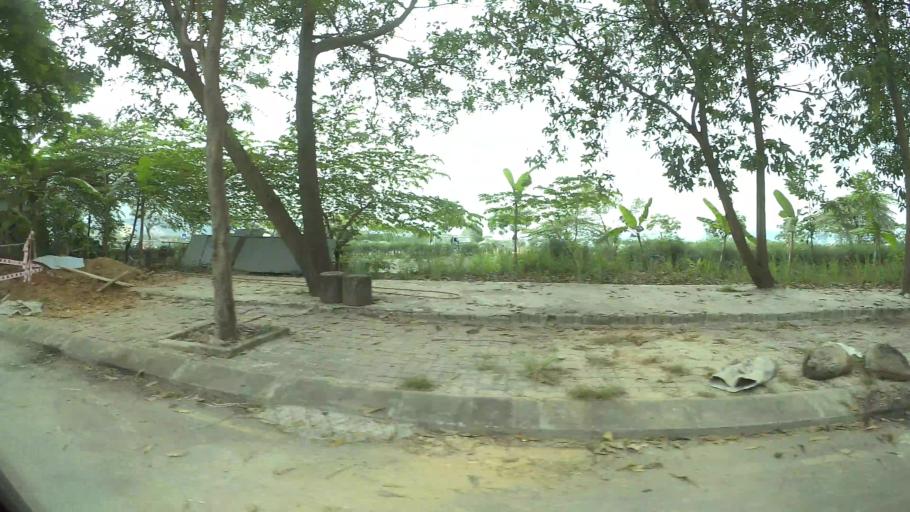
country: VN
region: Da Nang
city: Lien Chieu
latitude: 16.0723
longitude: 108.1640
